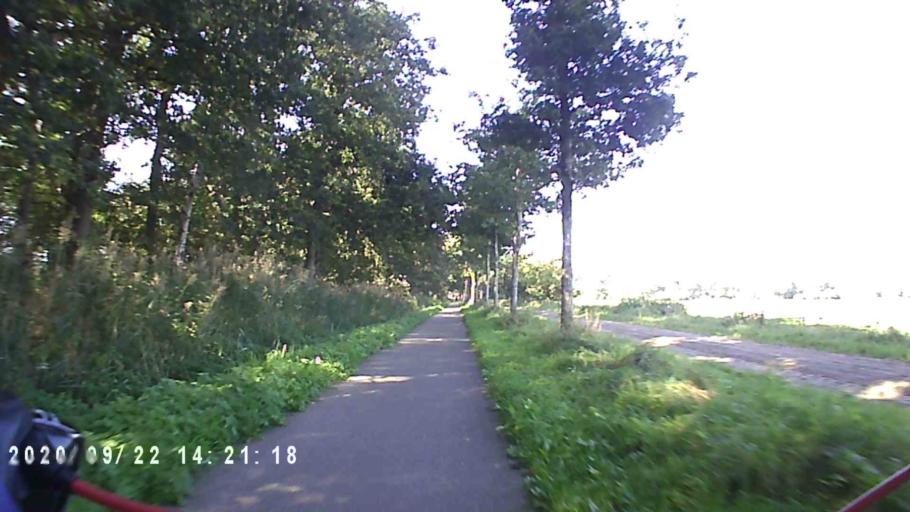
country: NL
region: Groningen
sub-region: Gemeente Leek
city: Leek
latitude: 53.0656
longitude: 6.4054
